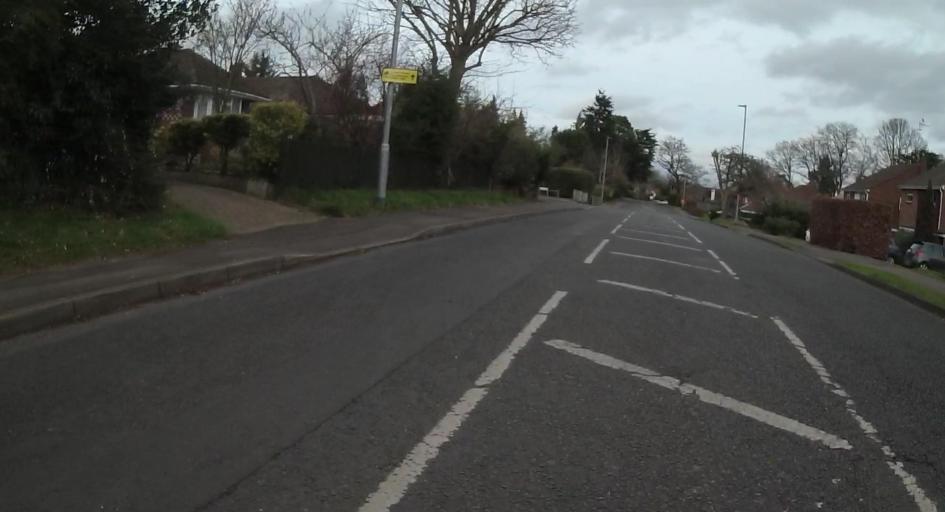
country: GB
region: England
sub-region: Wokingham
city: Wokingham
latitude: 51.4167
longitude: -0.8562
